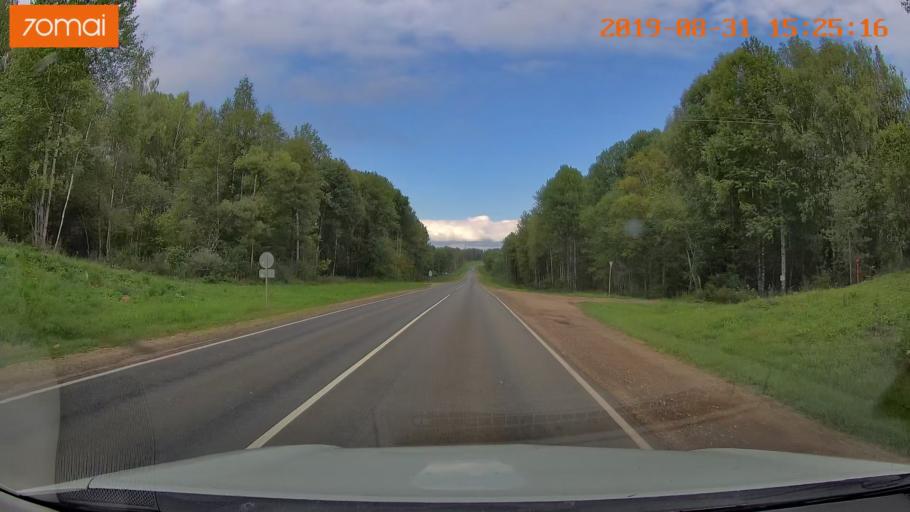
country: RU
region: Kaluga
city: Baryatino
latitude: 54.5390
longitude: 34.5170
